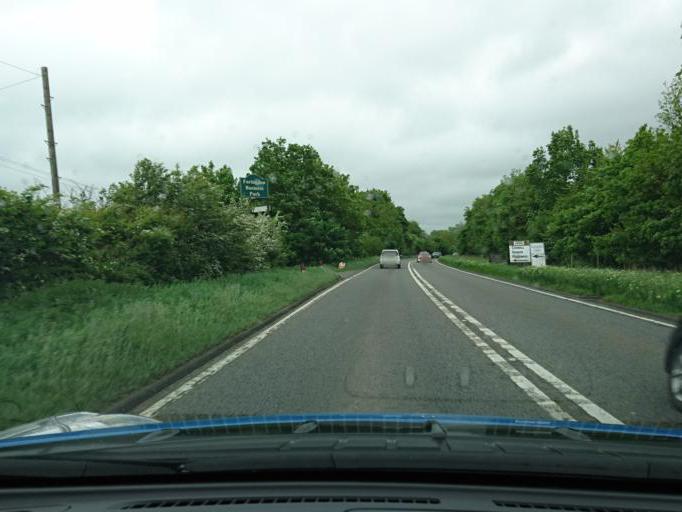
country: GB
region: England
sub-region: Oxfordshire
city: Faringdon
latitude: 51.6359
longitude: -1.6046
